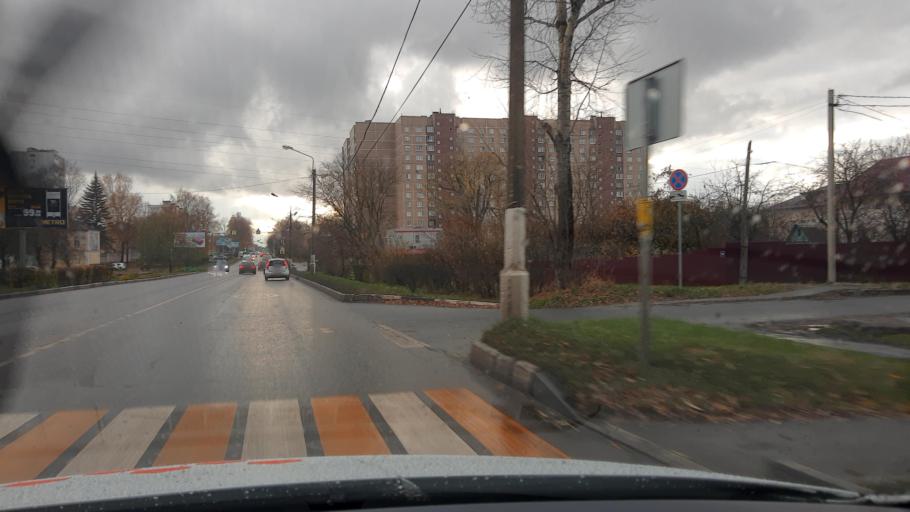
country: RU
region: Moskovskaya
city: Noginsk
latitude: 55.8454
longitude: 38.4118
